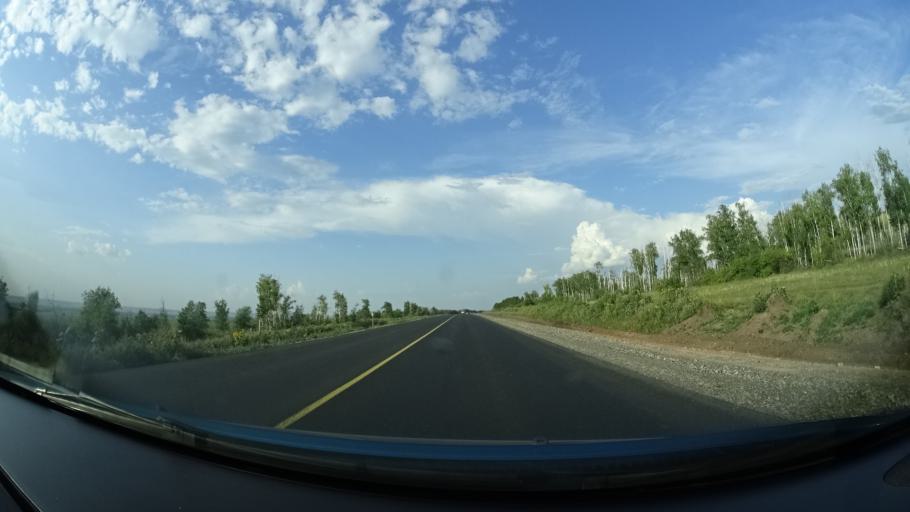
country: RU
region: Samara
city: Sukhodol
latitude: 53.7671
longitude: 50.8899
